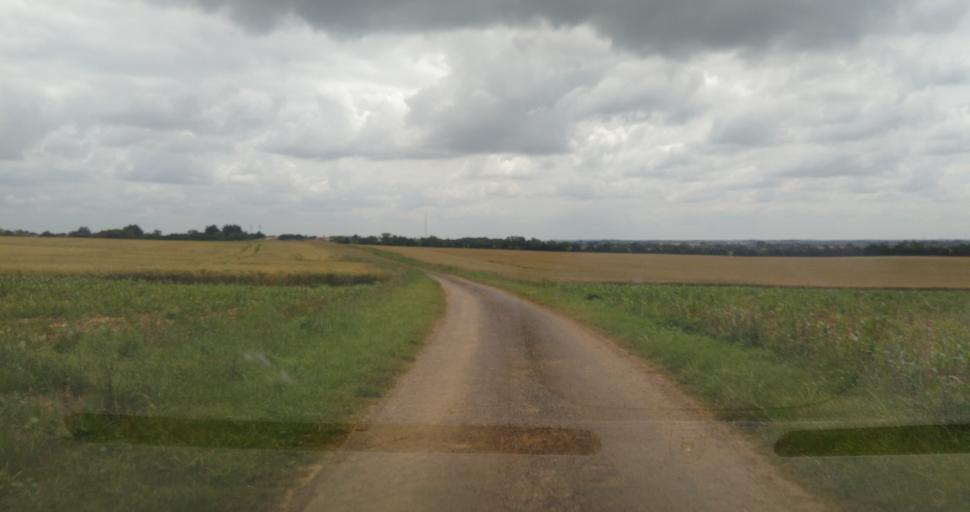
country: FR
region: Pays de la Loire
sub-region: Departement de la Vendee
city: Sainte-Gemme-la-Plaine
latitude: 46.5109
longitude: -1.0781
